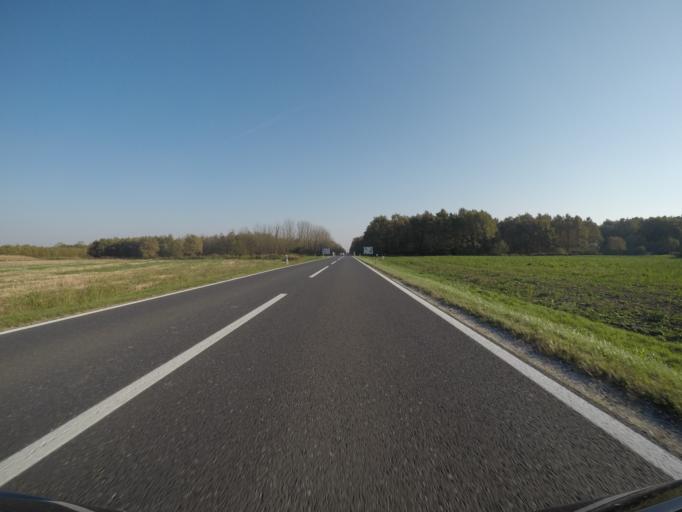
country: HR
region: Koprivnicko-Krizevacka
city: Kalinovac
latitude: 46.0000
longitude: 17.1166
